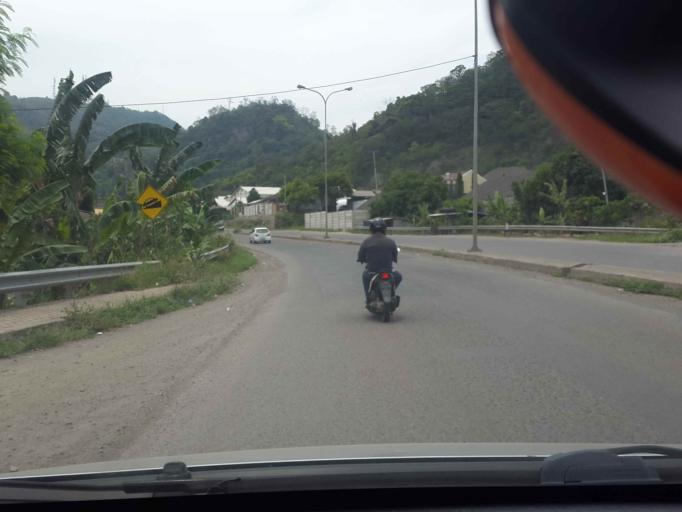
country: ID
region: Lampung
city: Panjang
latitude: -5.4487
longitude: 105.3134
